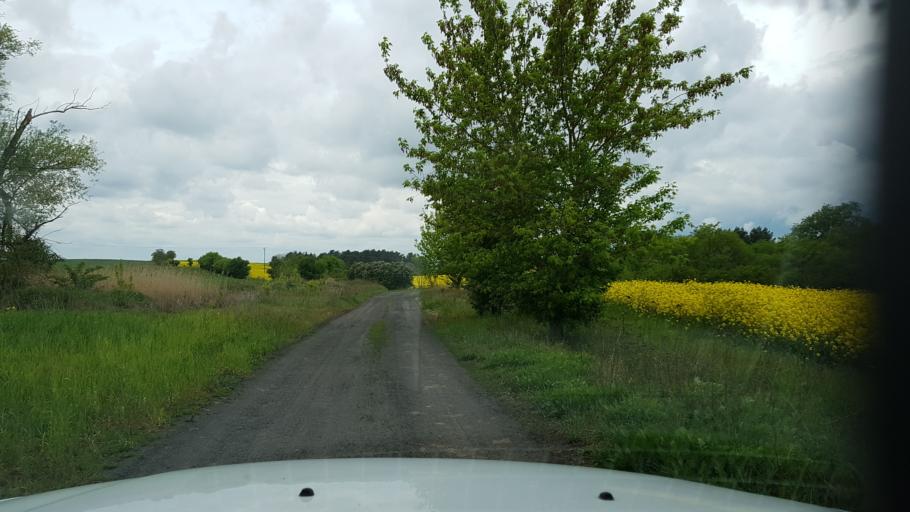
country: PL
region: West Pomeranian Voivodeship
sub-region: Powiat gryfinski
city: Mieszkowice
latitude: 52.8441
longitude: 14.4892
